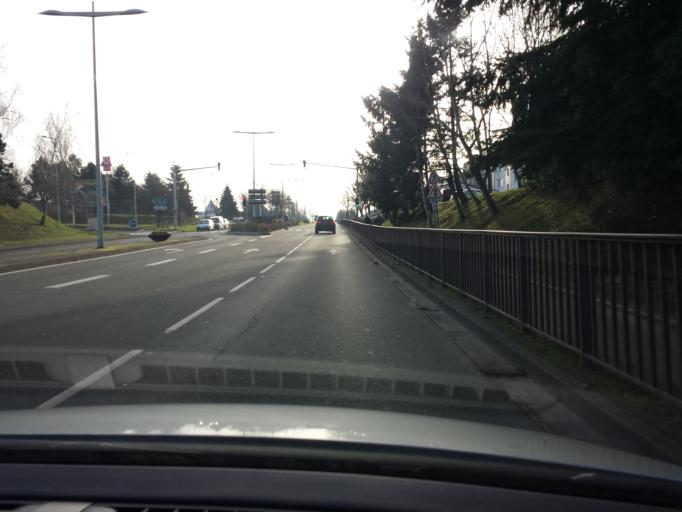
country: FR
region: Haute-Normandie
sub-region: Departement de l'Eure
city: Evreux
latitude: 49.0156
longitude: 1.1702
